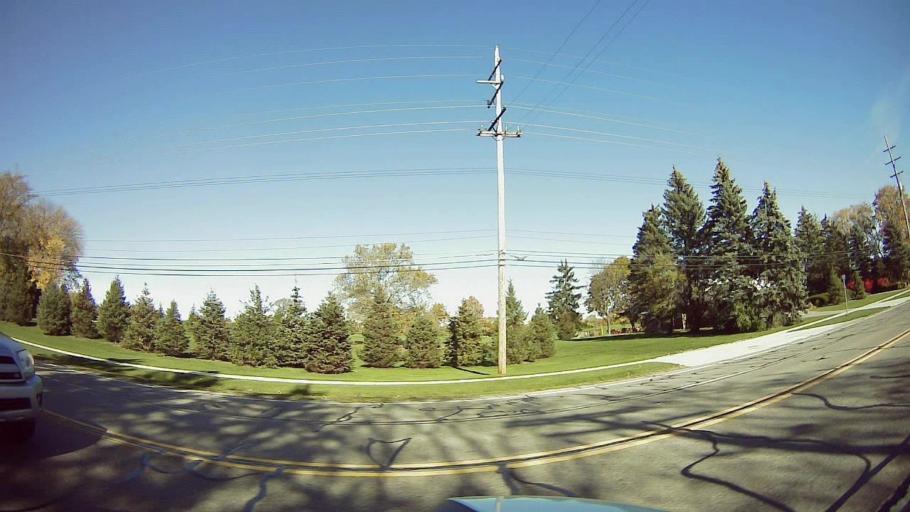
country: US
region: Michigan
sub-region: Oakland County
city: Bingham Farms
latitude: 42.5451
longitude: -83.2723
